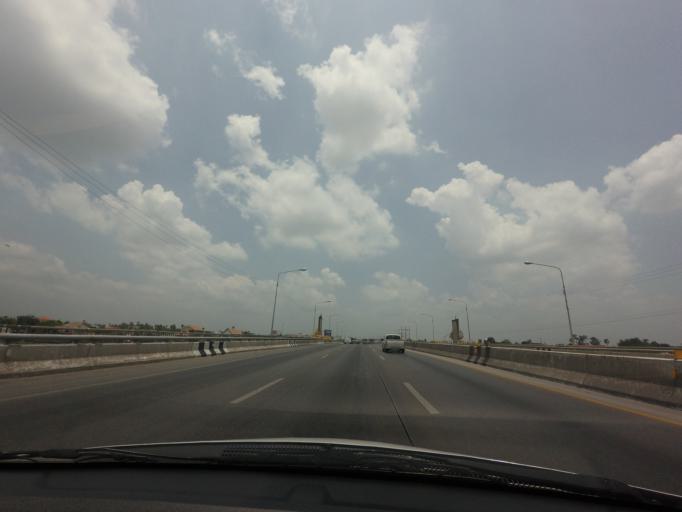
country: TH
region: Pathum Thani
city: Pathum Thani
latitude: 14.0255
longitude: 100.5392
